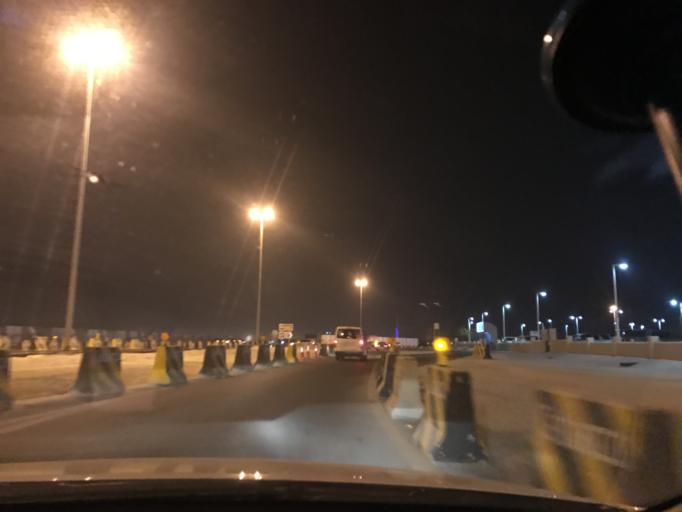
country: BH
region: Muharraq
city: Al Muharraq
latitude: 26.3048
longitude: 50.6273
